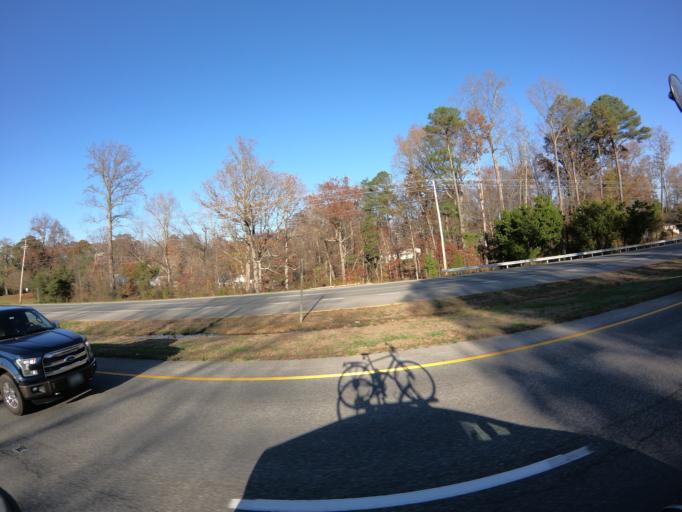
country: US
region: Maryland
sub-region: Saint Mary's County
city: Golden Beach
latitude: 38.4002
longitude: -76.6614
